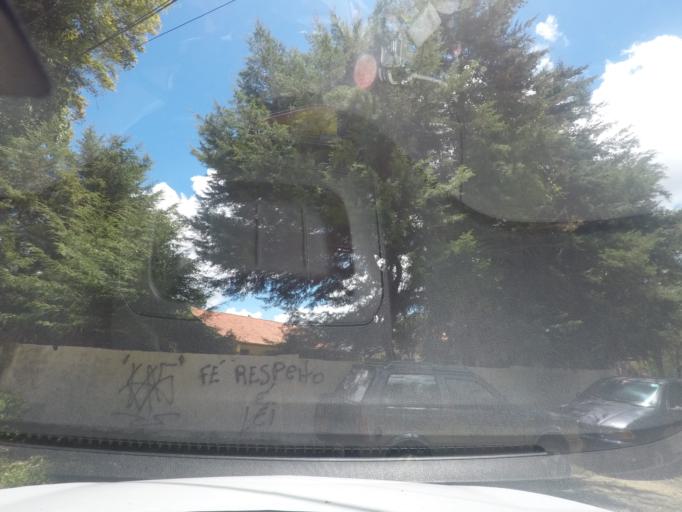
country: BR
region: Rio de Janeiro
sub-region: Teresopolis
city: Teresopolis
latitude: -22.4331
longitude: -42.9830
